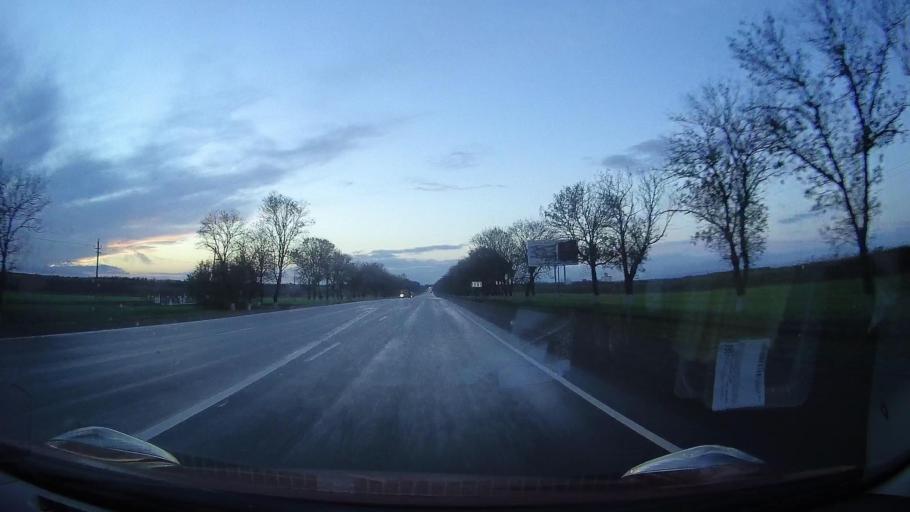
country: RU
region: Krasnodarskiy
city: Uspenskoye
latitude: 44.8228
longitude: 41.3581
